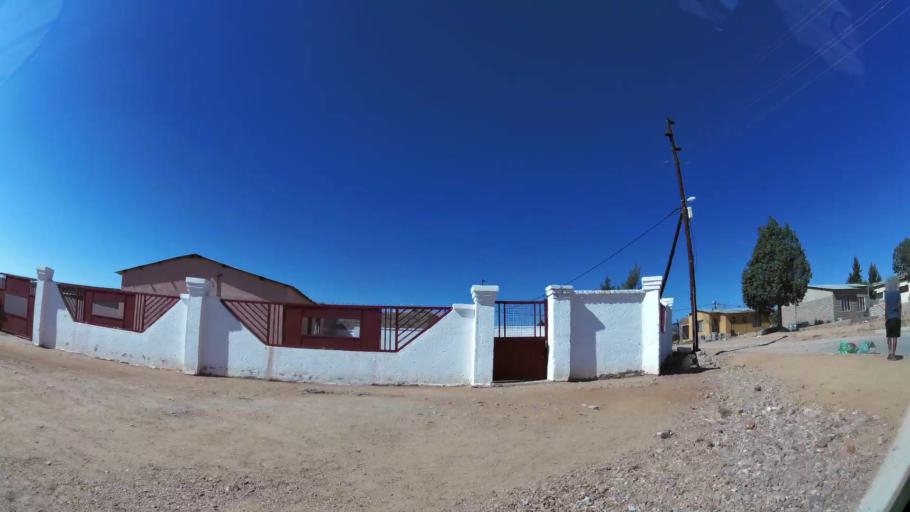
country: ZA
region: Limpopo
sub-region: Capricorn District Municipality
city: Polokwane
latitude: -23.8783
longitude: 29.4118
